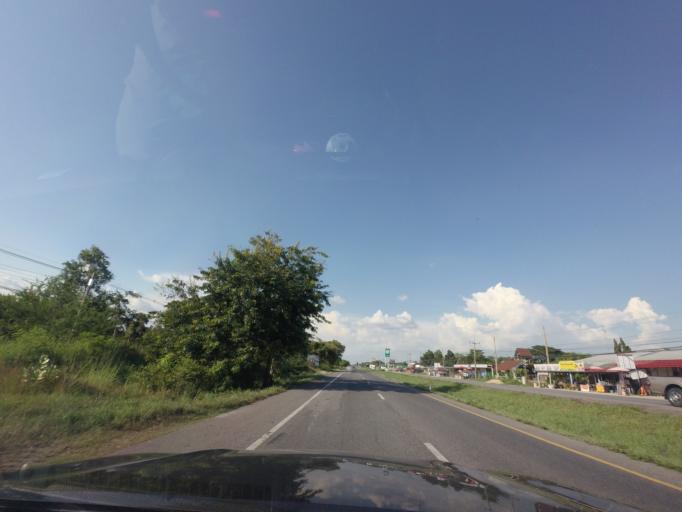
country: TH
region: Khon Kaen
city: Non Sila
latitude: 15.9912
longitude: 102.6989
